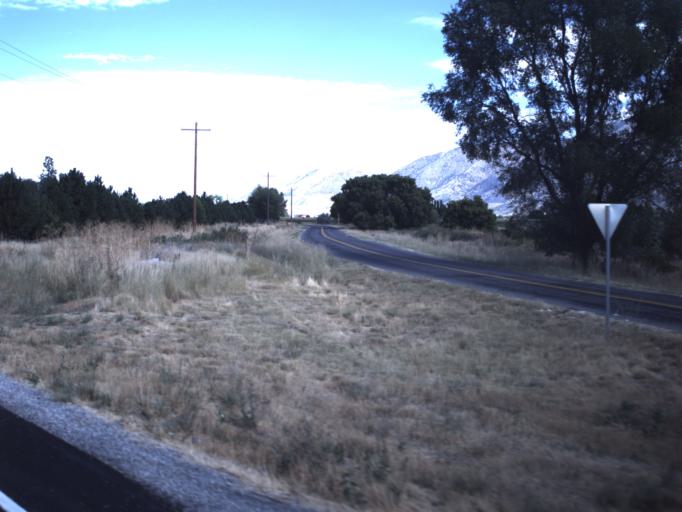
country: US
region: Utah
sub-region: Box Elder County
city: Honeyville
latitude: 41.6372
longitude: -112.1289
